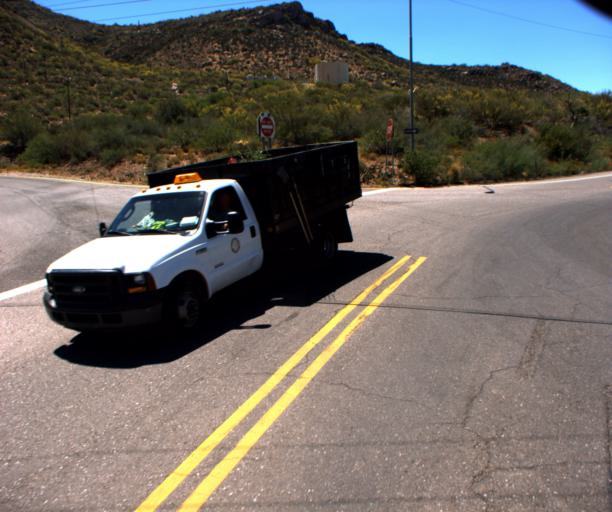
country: US
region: Arizona
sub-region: Pinal County
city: Superior
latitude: 33.2923
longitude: -111.0960
